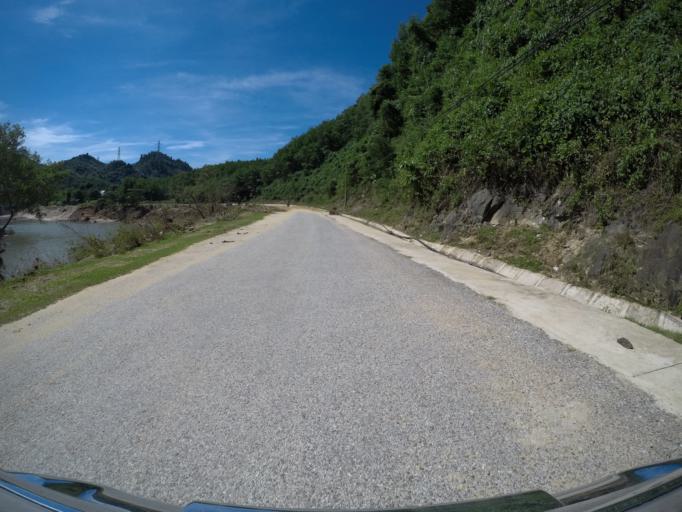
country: VN
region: Quang Nam
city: Thanh My
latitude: 15.6904
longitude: 107.7615
